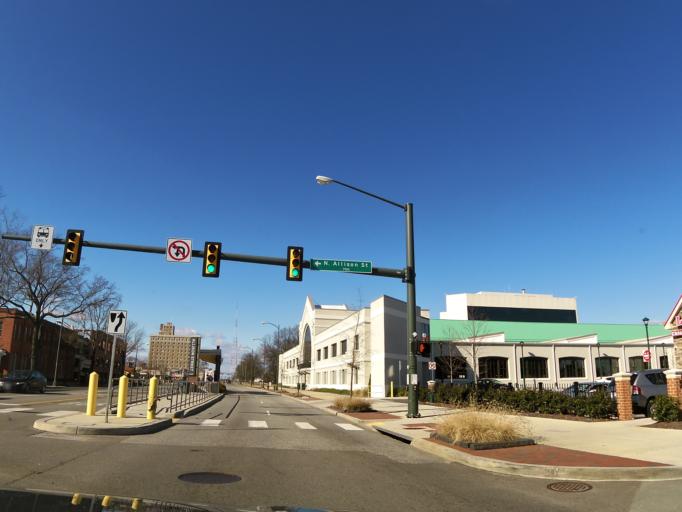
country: US
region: Virginia
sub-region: City of Richmond
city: Richmond
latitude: 37.5579
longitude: -77.4624
